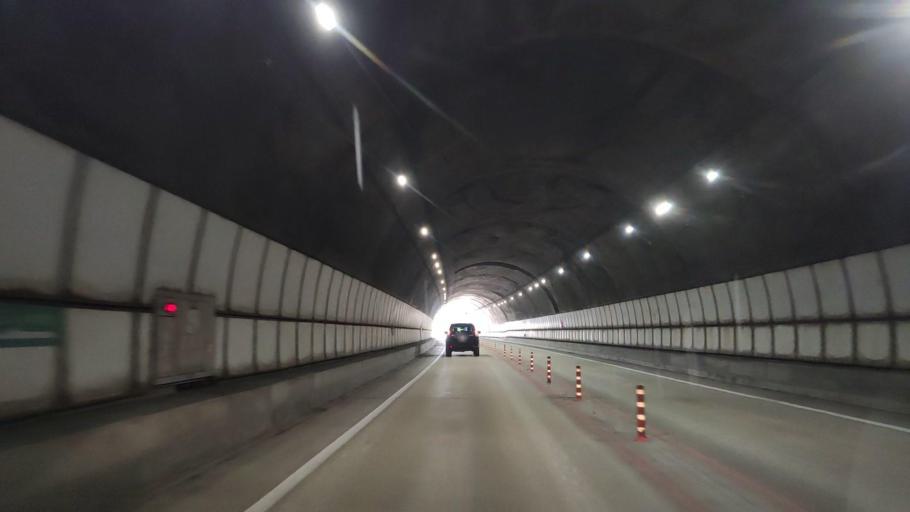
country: JP
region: Yamagata
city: Shinjo
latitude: 38.6791
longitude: 140.3191
